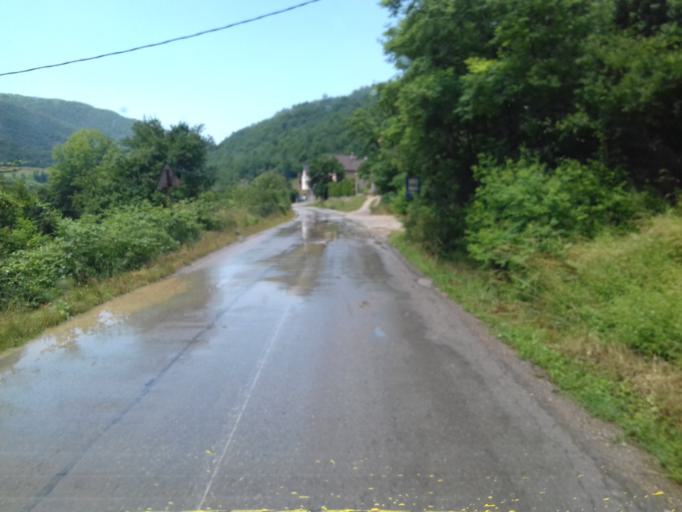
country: BA
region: Federation of Bosnia and Herzegovina
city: Visoko
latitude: 43.9543
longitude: 18.1406
